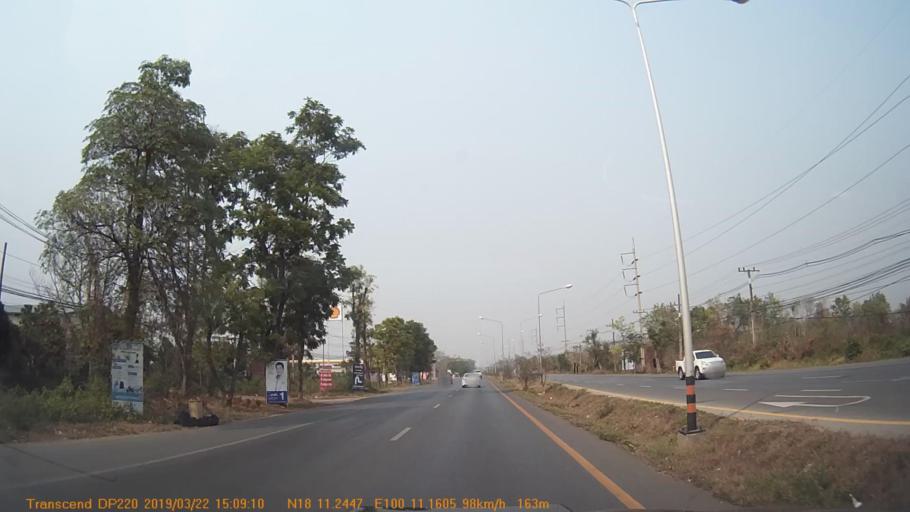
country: TH
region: Phrae
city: Phrae
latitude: 18.1877
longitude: 100.1862
